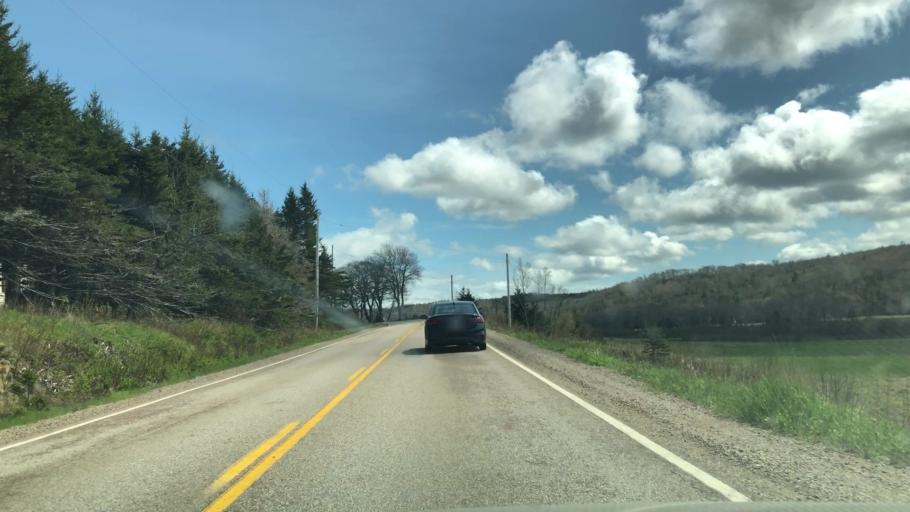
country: CA
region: Nova Scotia
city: Antigonish
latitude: 45.2028
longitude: -62.0036
